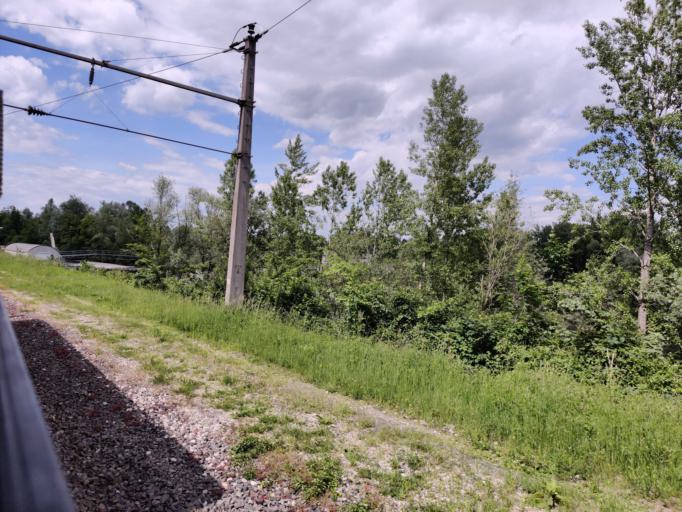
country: AT
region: Styria
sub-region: Politischer Bezirk Leibnitz
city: Retznei
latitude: 46.7430
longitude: 15.5709
